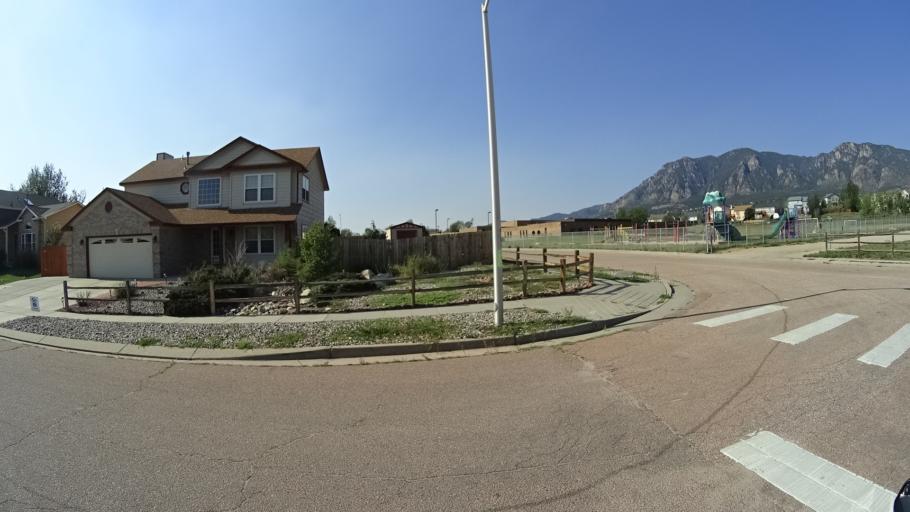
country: US
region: Colorado
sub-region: El Paso County
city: Stratmoor
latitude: 38.7718
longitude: -104.8050
